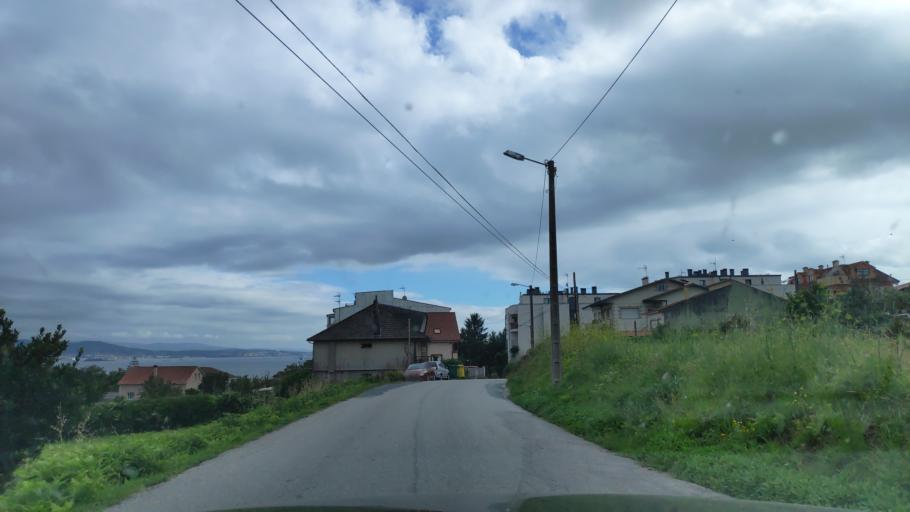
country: ES
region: Galicia
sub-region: Provincia da Coruna
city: Rianxo
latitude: 42.6478
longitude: -8.8138
